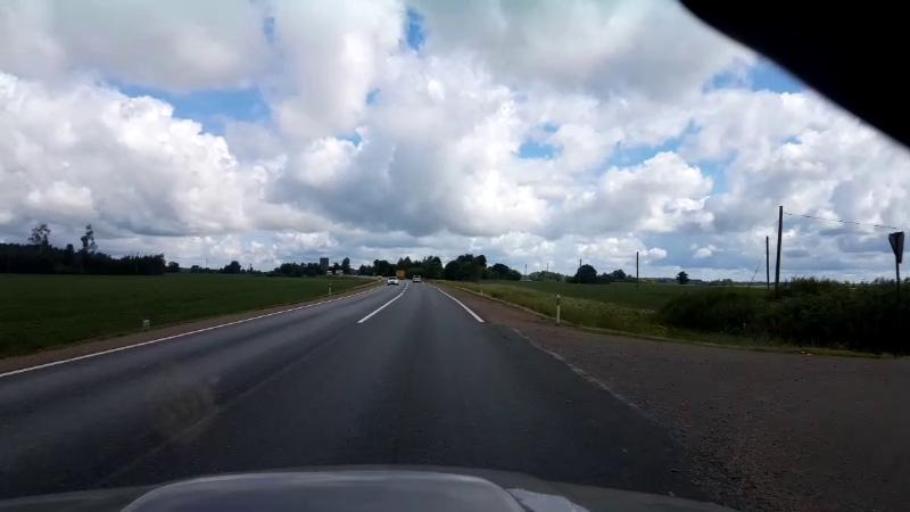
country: LV
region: Bauskas Rajons
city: Bauska
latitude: 56.4840
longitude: 24.1770
